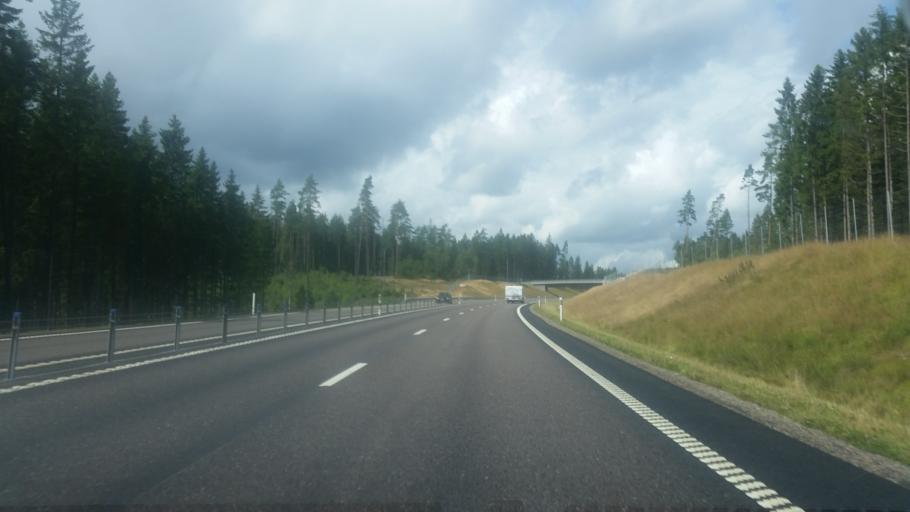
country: SE
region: Vaestra Goetaland
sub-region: Boras Kommun
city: Sjomarken
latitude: 57.7010
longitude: 12.8808
